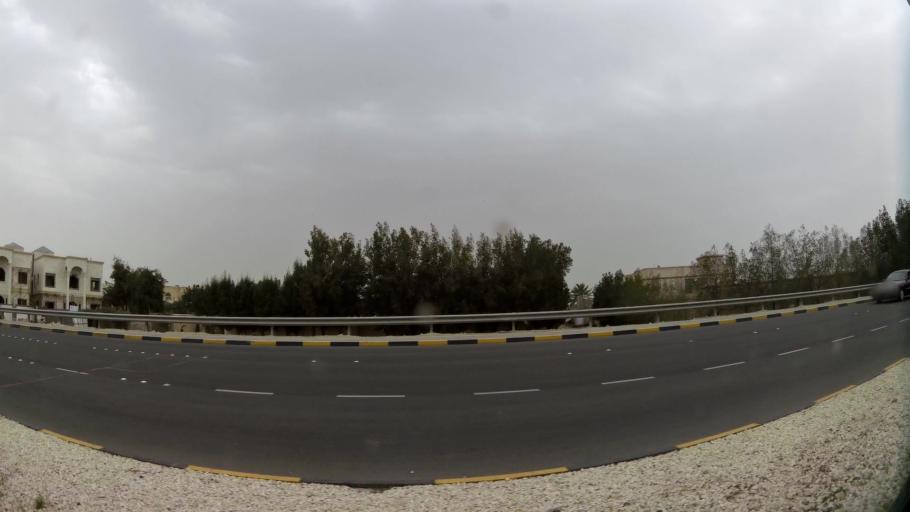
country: BH
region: Northern
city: Ar Rifa'
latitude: 26.1351
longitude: 50.5430
